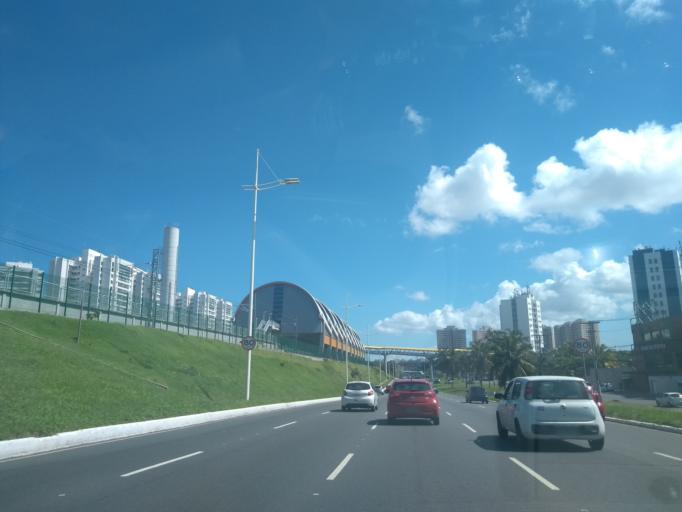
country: BR
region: Bahia
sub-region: Lauro De Freitas
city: Lauro de Freitas
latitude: -12.9374
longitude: -38.4040
